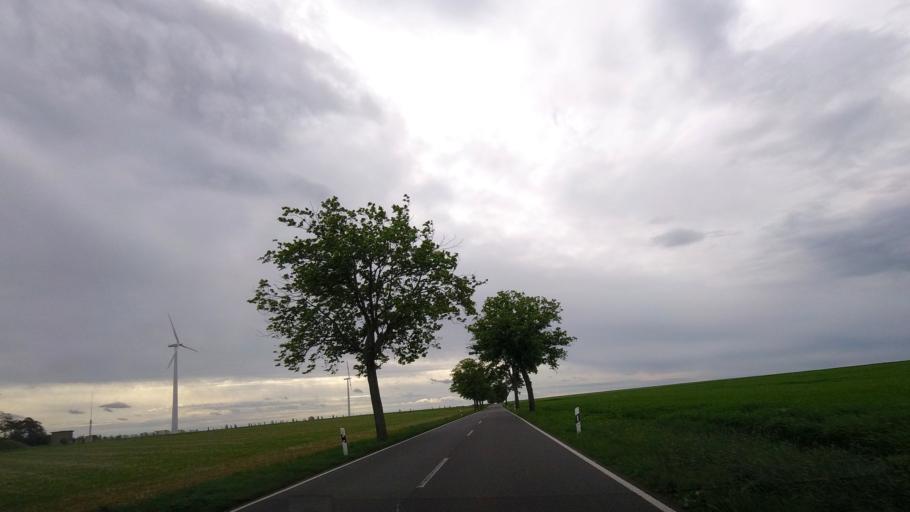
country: DE
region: Brandenburg
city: Ihlow
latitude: 51.9300
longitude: 13.2053
